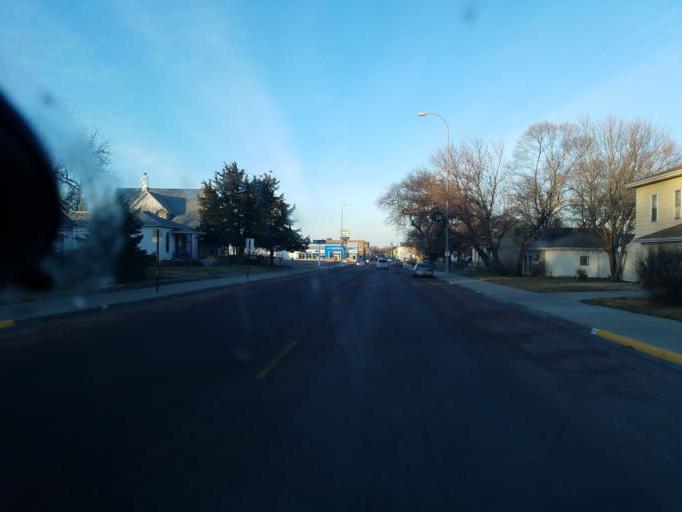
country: US
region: South Dakota
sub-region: Davison County
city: Mitchell
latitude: 43.7095
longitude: -98.0200
